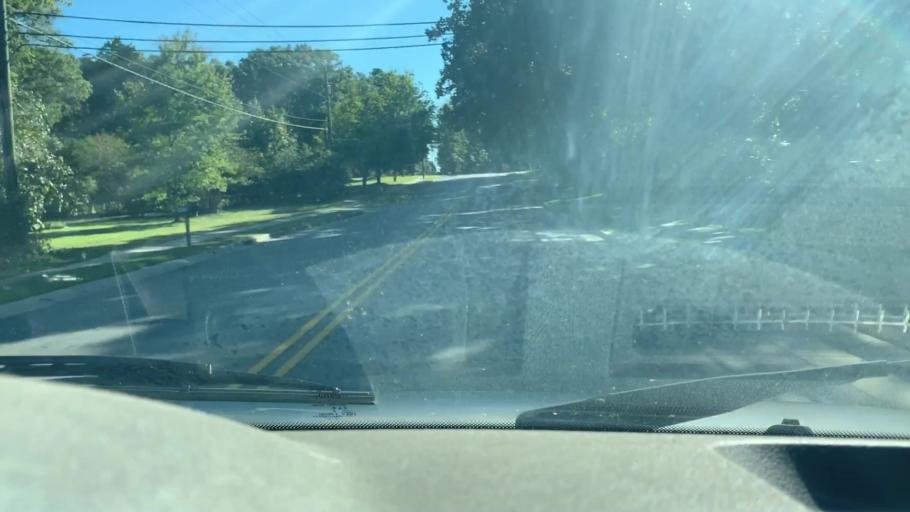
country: US
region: North Carolina
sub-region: Mecklenburg County
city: Charlotte
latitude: 35.2904
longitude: -80.7864
